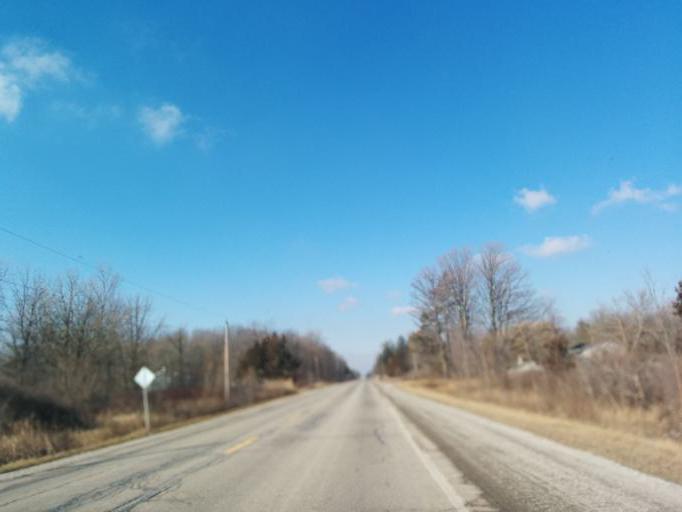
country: CA
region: Ontario
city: Brantford
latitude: 43.0130
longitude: -80.1899
